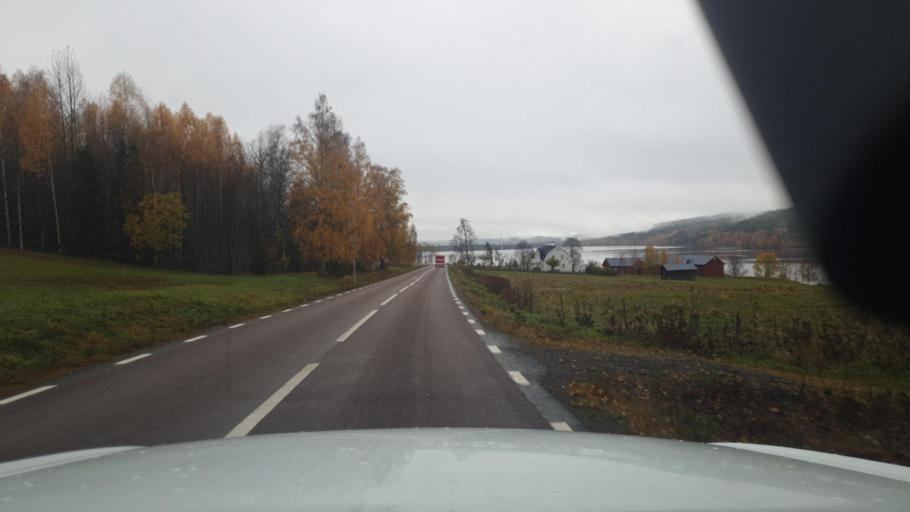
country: SE
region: Vaermland
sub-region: Sunne Kommun
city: Sunne
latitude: 59.8905
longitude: 12.9201
